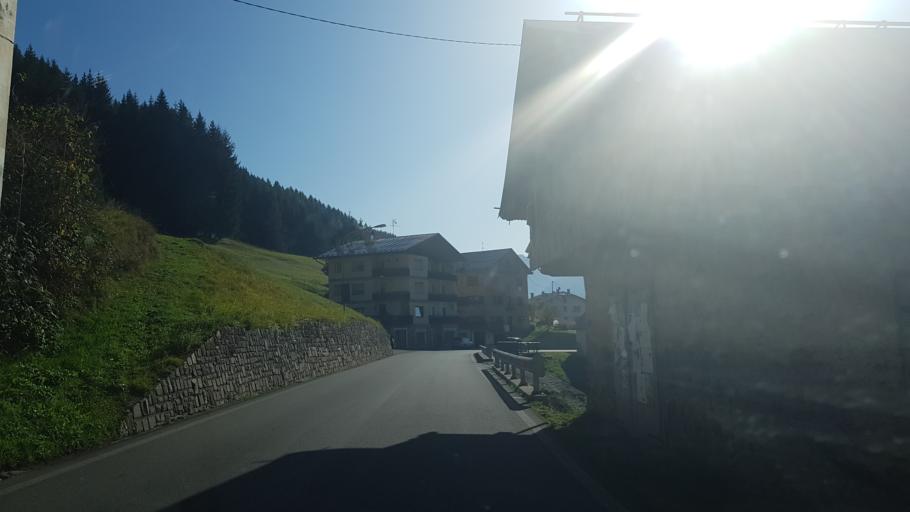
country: IT
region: Veneto
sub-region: Provincia di Belluno
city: Candide
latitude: 46.5987
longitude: 12.4953
